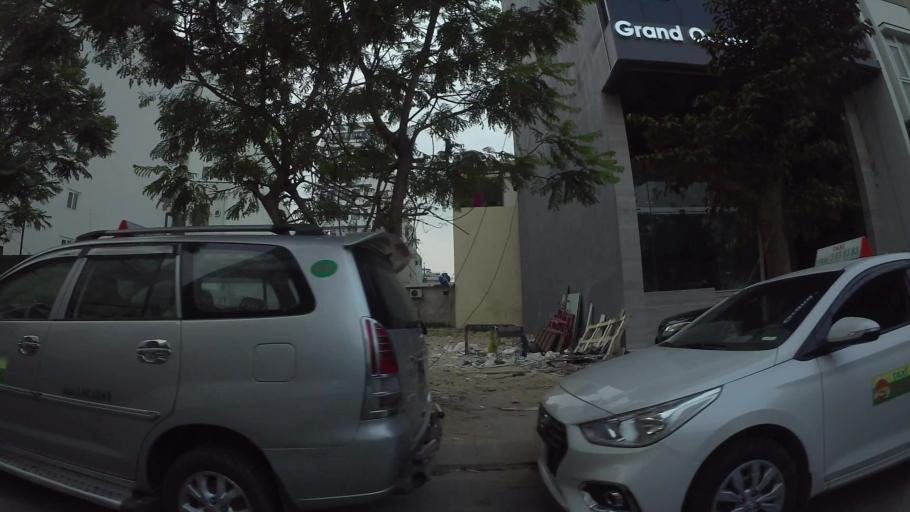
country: VN
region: Da Nang
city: Son Tra
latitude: 16.0548
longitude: 108.2449
